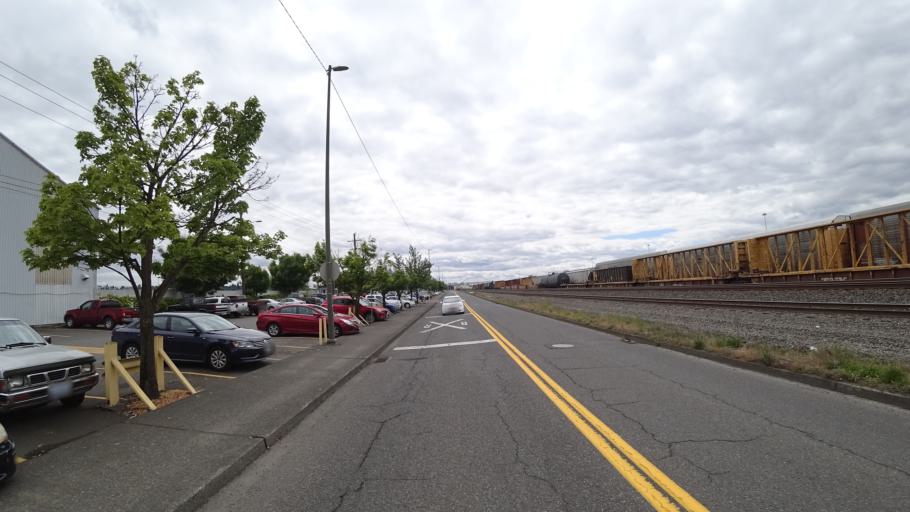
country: US
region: Oregon
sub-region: Multnomah County
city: Portland
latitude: 45.5532
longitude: -122.7183
